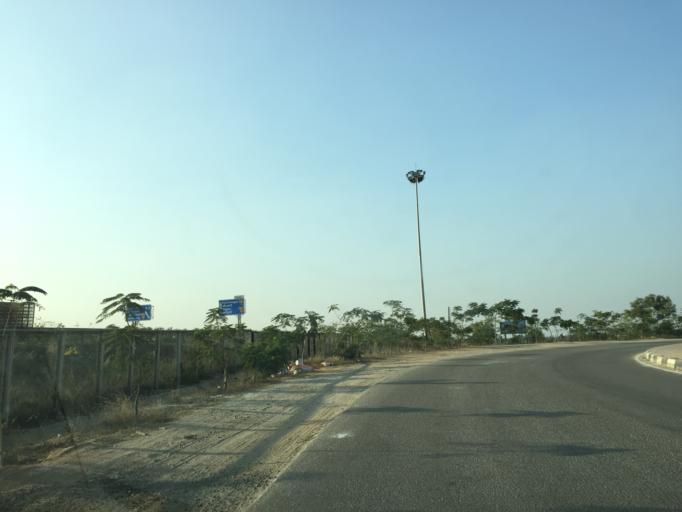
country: IN
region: Telangana
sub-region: Rangareddi
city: Ghatkesar
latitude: 17.4381
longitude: 78.6719
